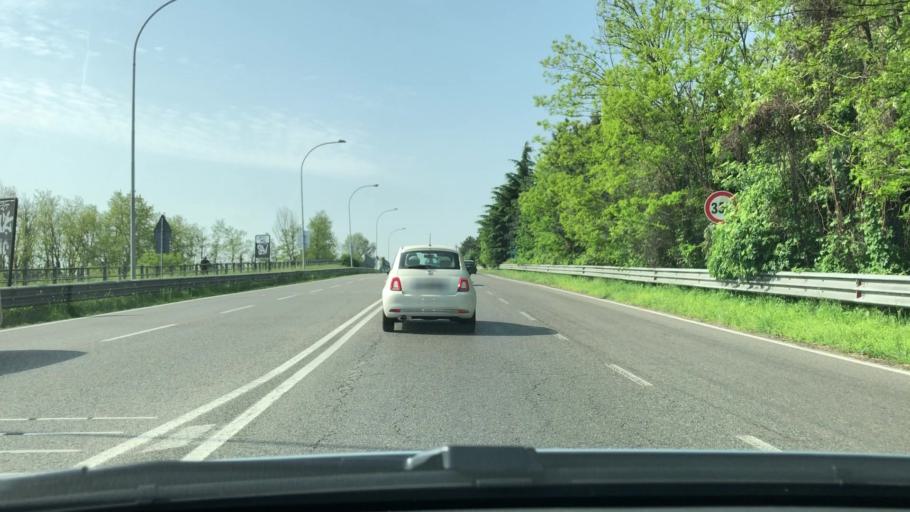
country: IT
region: Lombardy
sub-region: Provincia di Monza e Brianza
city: Meda
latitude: 45.6571
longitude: 9.1554
